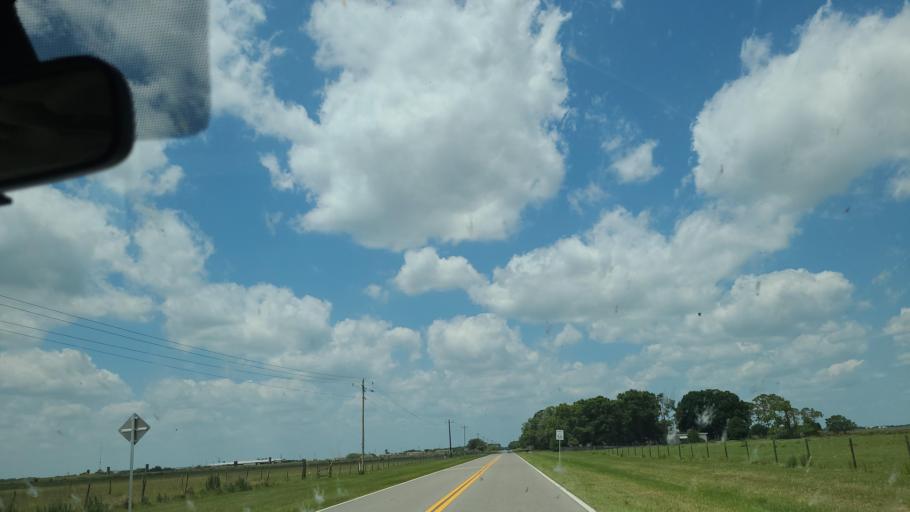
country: US
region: Florida
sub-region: Okeechobee County
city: Cypress Quarters
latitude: 27.3906
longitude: -80.8181
